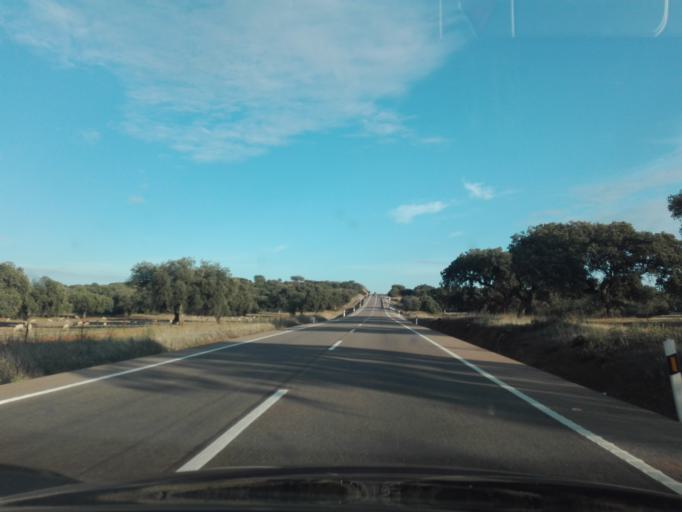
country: ES
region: Extremadura
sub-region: Provincia de Badajoz
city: Usagre
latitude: 38.3673
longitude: -6.2382
